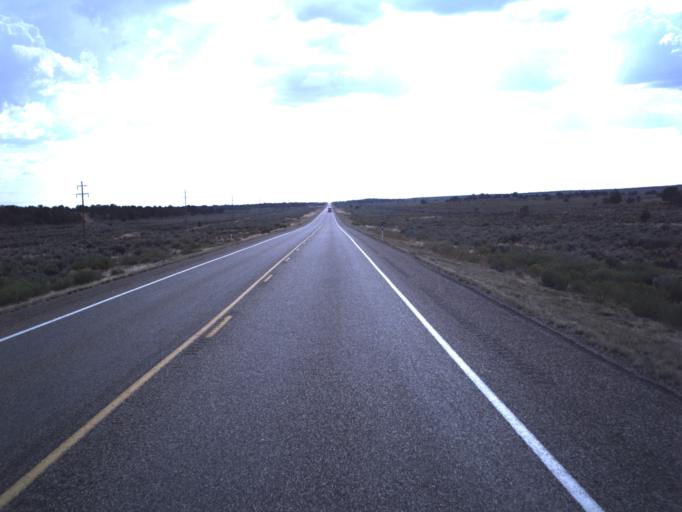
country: US
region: Utah
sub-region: Kane County
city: Kanab
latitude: 37.1044
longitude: -112.1269
